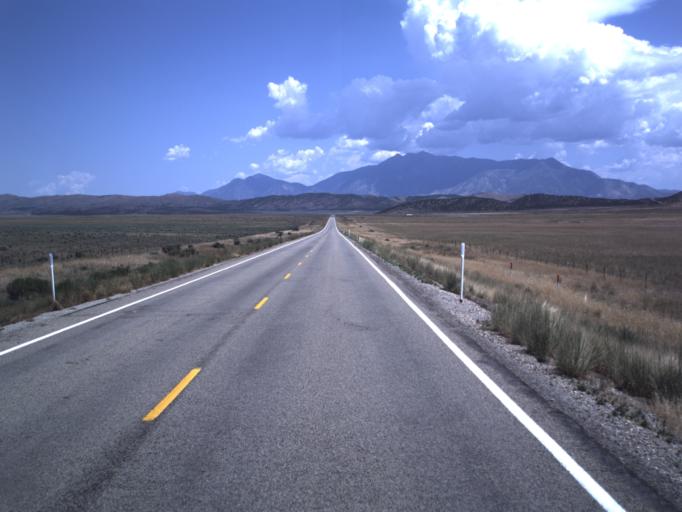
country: US
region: Utah
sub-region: Juab County
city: Nephi
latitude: 39.6721
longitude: -112.0281
